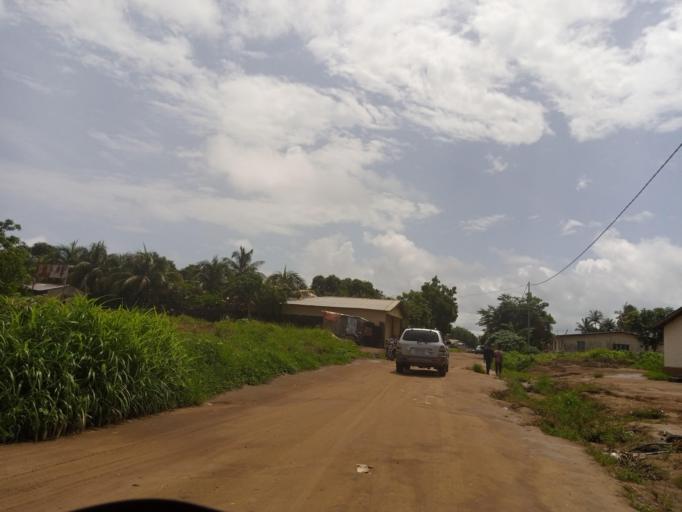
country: SL
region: Northern Province
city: Tintafor
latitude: 8.6264
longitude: -13.2115
